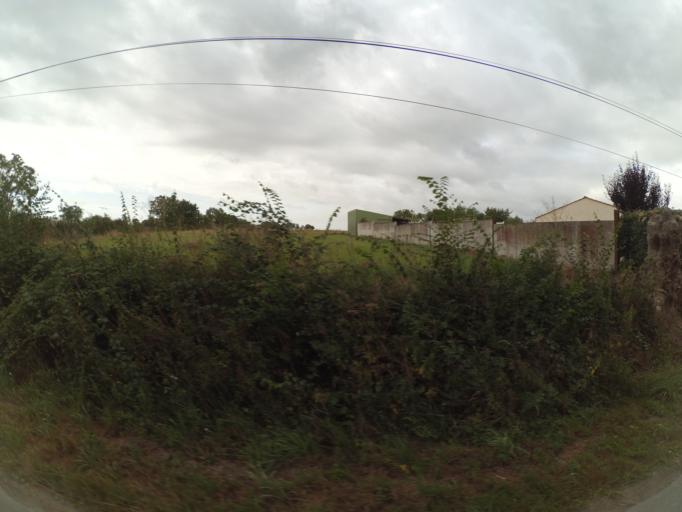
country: FR
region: Pays de la Loire
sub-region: Departement de la Vendee
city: Saint-Hilaire-de-Loulay
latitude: 47.0274
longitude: -1.3254
